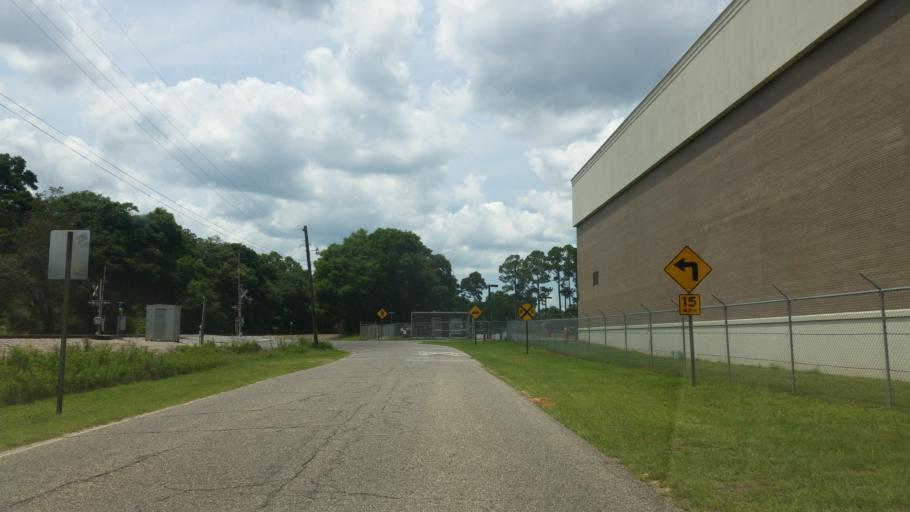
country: US
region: Florida
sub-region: Escambia County
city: Brent
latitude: 30.4724
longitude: -87.2380
